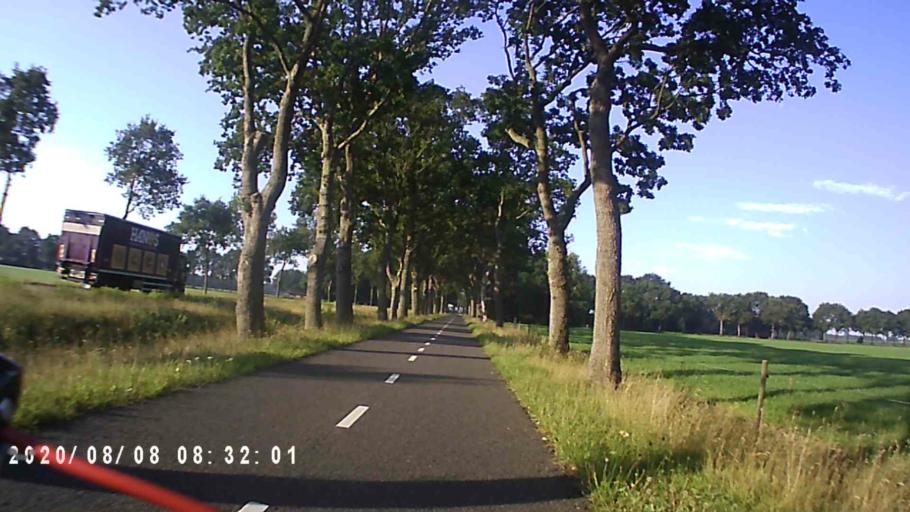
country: NL
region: Groningen
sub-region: Gemeente Leek
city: Leek
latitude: 53.0771
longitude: 6.3338
